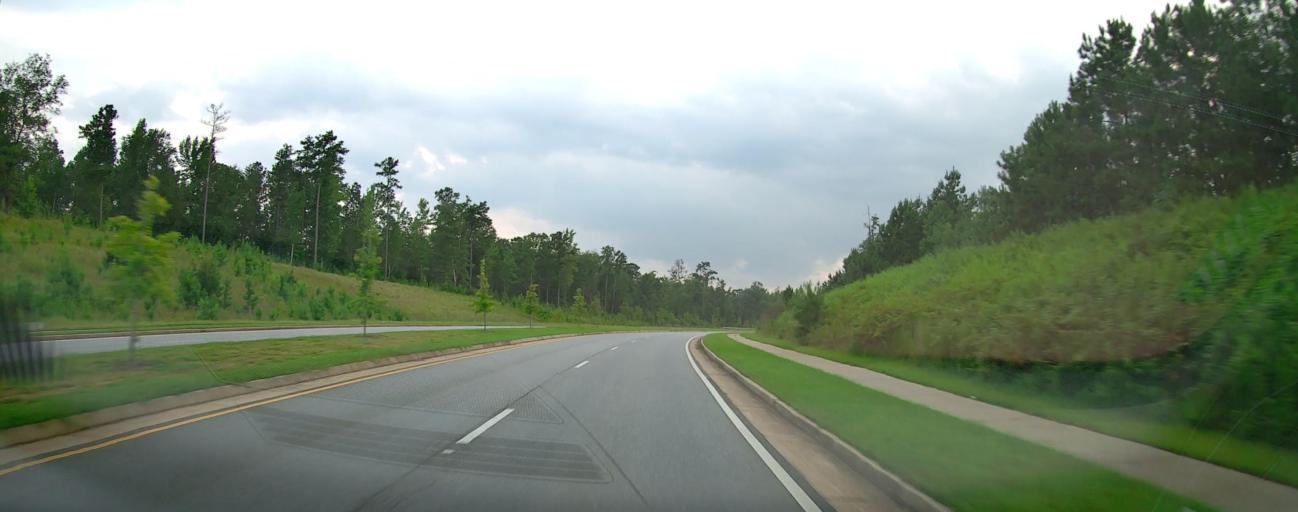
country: US
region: Georgia
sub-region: Muscogee County
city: Columbus
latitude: 32.5133
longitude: -84.8473
